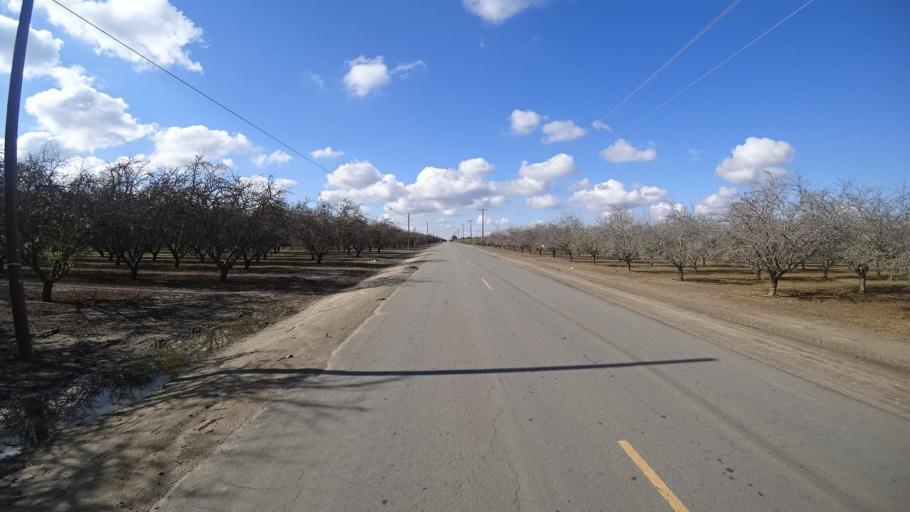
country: US
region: California
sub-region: Kern County
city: McFarland
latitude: 35.6887
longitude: -119.2886
